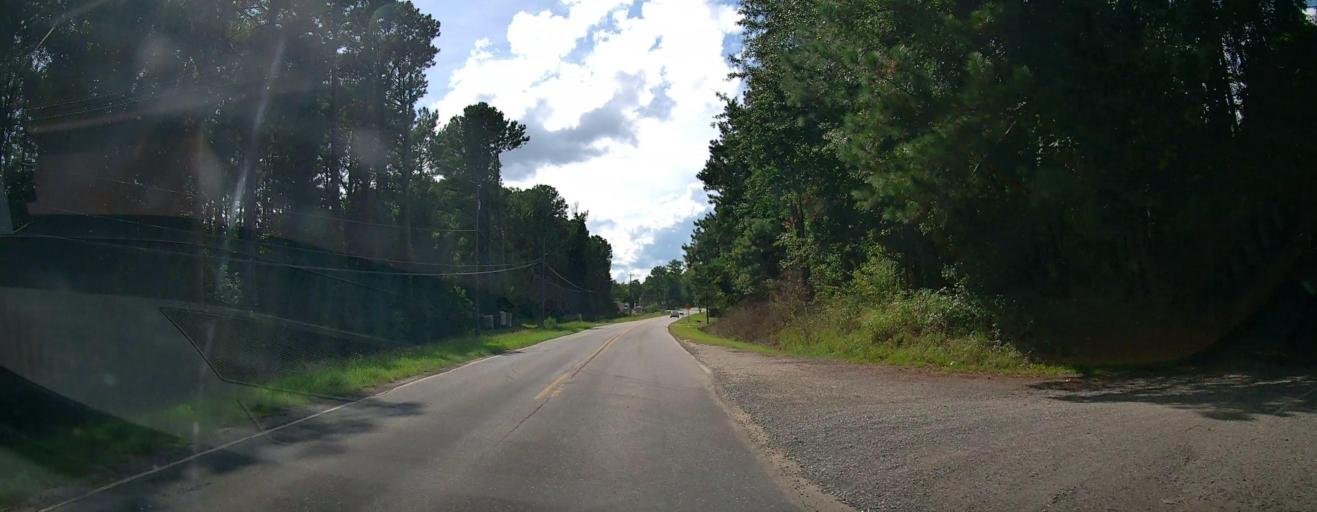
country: US
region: Alabama
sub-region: Russell County
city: Phenix City
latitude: 32.5929
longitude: -84.9418
